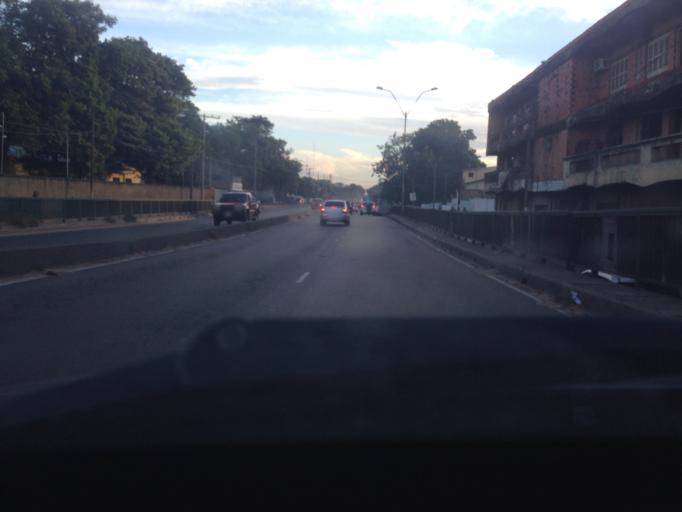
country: PY
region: Central
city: Lambare
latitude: -25.3400
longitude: -57.5854
